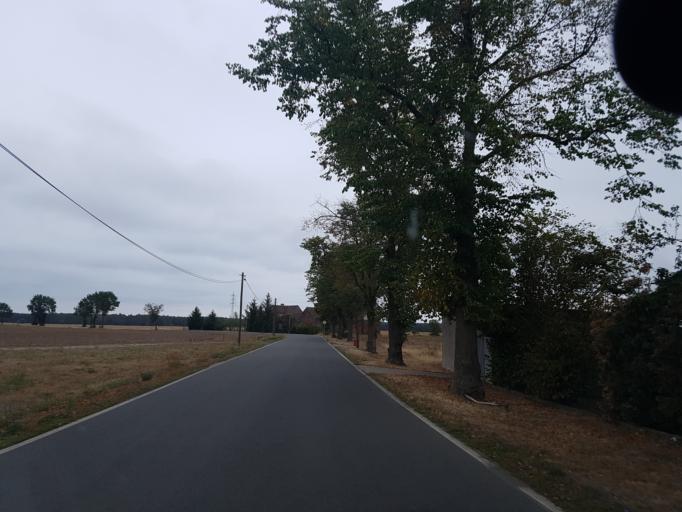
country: DE
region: Saxony-Anhalt
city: Annaburg
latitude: 51.7786
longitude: 13.0543
